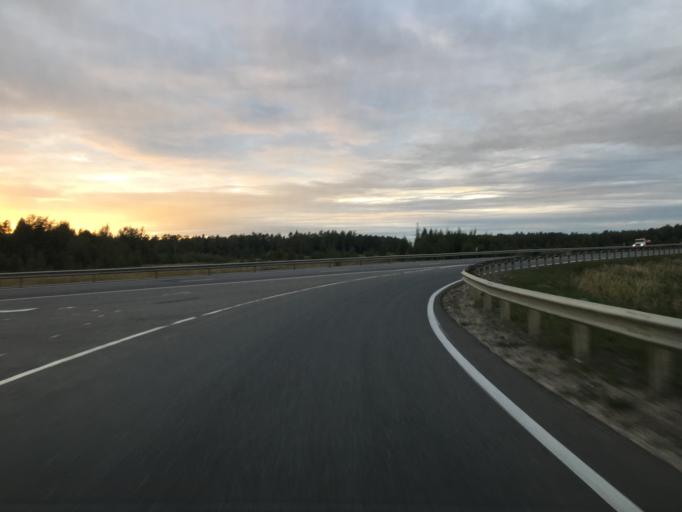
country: RU
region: Kaluga
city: Kaluga
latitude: 54.5683
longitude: 36.3352
